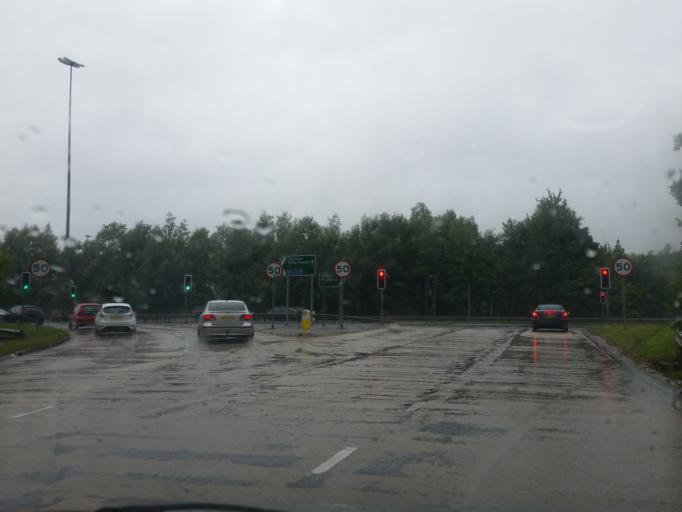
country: GB
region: Northern Ireland
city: Holywood
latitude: 54.6180
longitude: -5.8612
